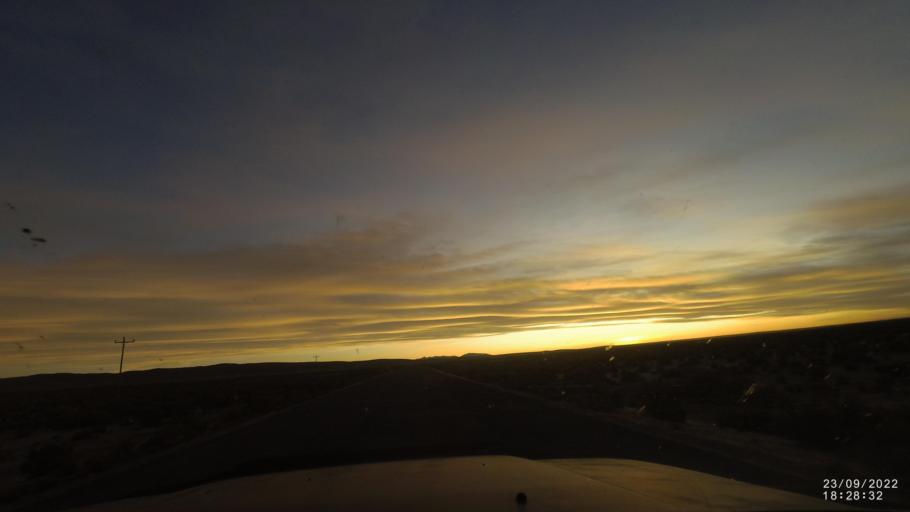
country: BO
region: Oruro
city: Challapata
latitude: -19.3382
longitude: -67.1786
